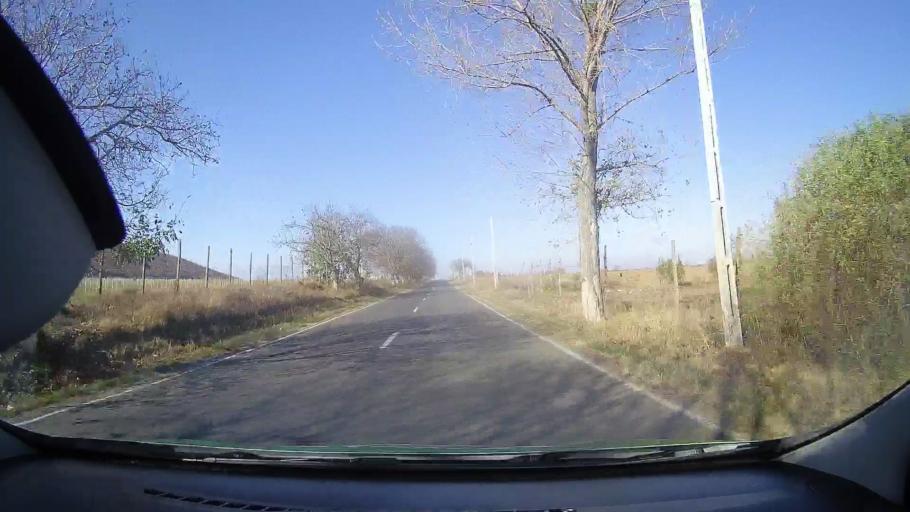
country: RO
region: Tulcea
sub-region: Oras Babadag
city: Babadag
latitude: 44.8823
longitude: 28.7428
